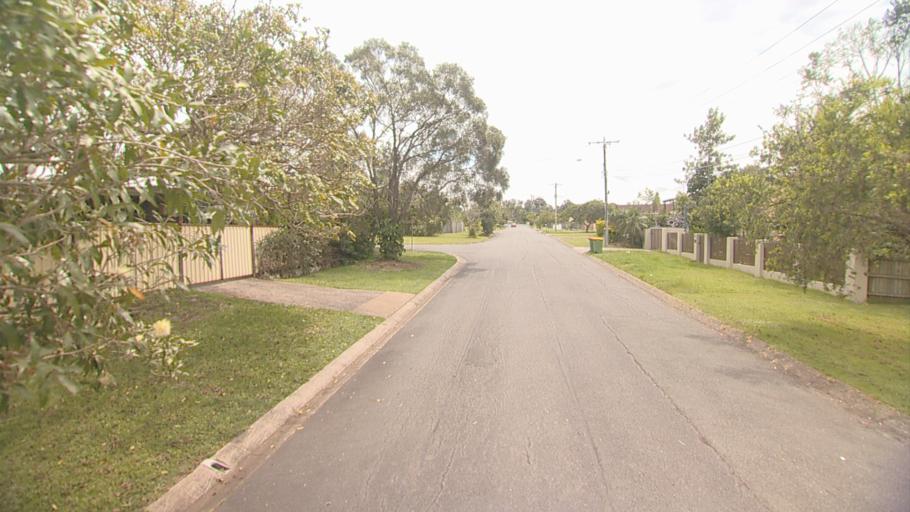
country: AU
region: Queensland
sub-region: Logan
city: Slacks Creek
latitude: -27.6499
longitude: 153.1503
